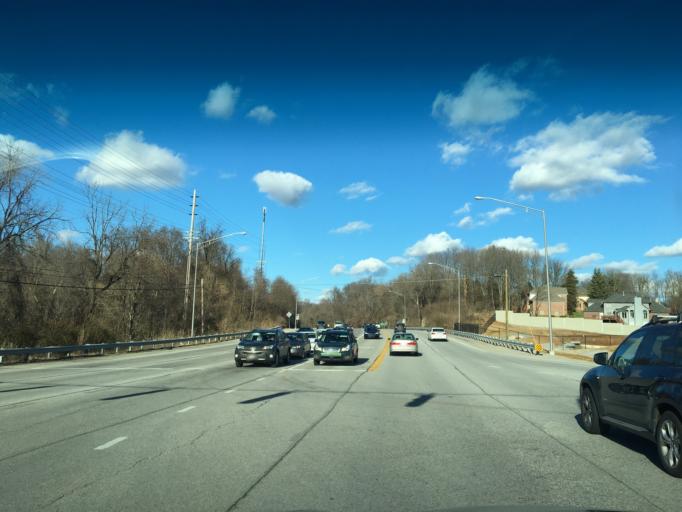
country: US
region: Kentucky
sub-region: Jefferson County
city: Prospect
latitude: 38.3233
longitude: -85.6219
